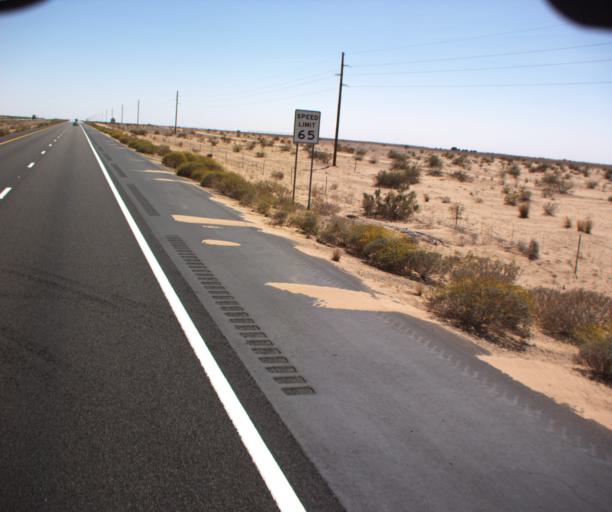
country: US
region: Arizona
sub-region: Yuma County
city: Somerton
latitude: 32.5281
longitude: -114.5622
